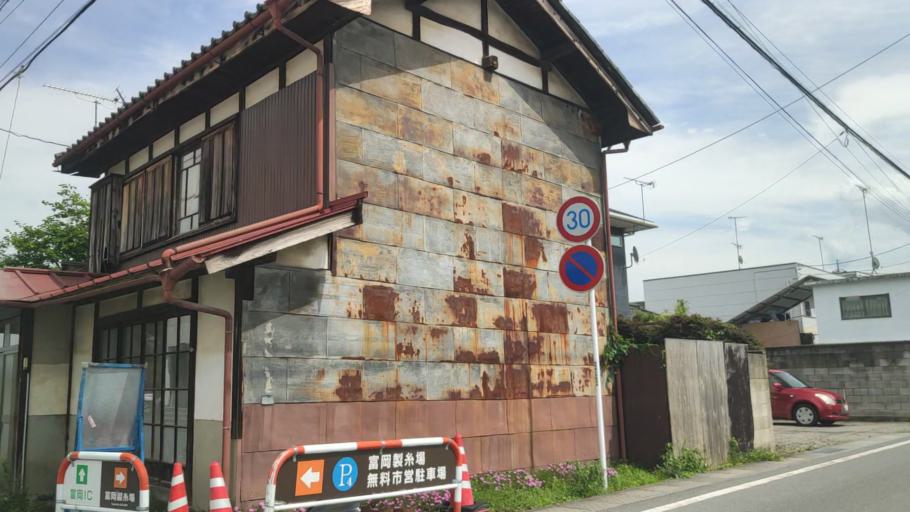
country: JP
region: Gunma
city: Tomioka
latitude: 36.2598
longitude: 138.8929
